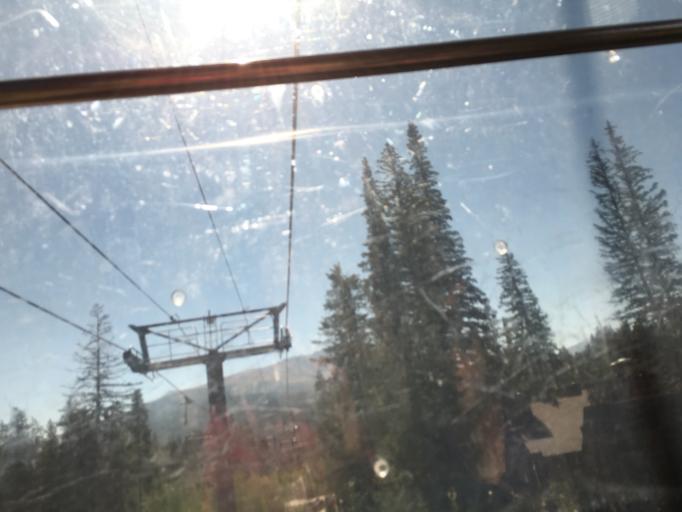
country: US
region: Colorado
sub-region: Summit County
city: Breckenridge
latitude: 39.4883
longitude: -106.0548
